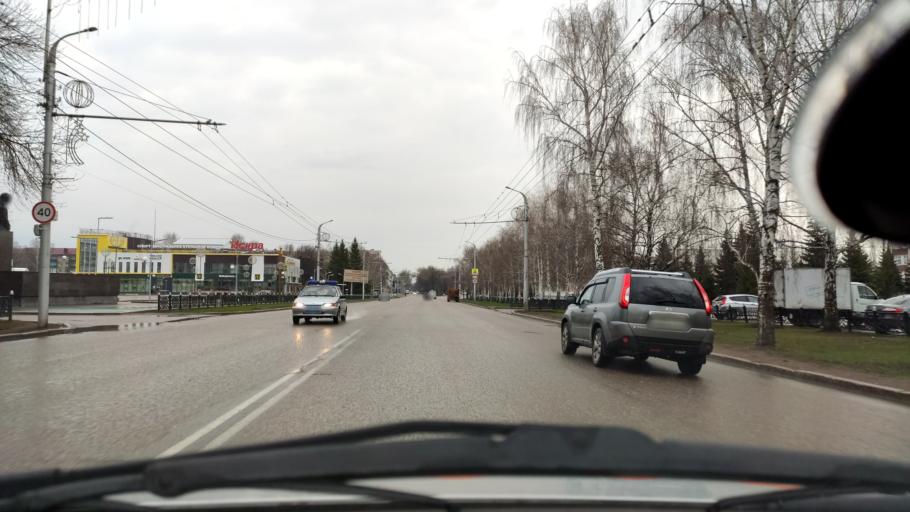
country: RU
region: Bashkortostan
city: Sterlitamak
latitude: 53.6359
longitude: 55.9356
